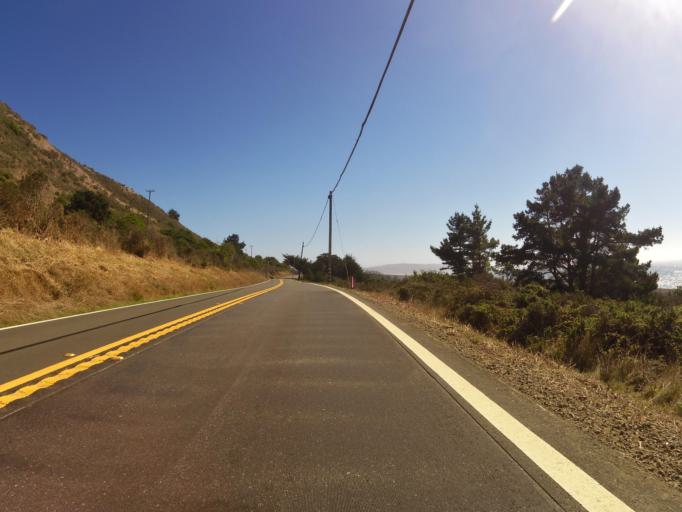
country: US
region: California
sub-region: Mendocino County
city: Fort Bragg
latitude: 39.5973
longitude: -123.7834
